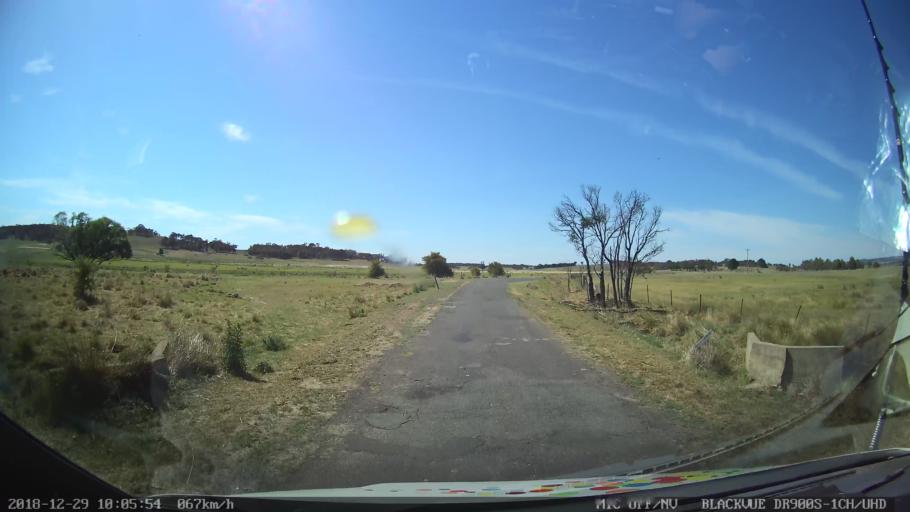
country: AU
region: New South Wales
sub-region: Goulburn Mulwaree
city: Goulburn
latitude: -34.8377
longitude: 149.4543
